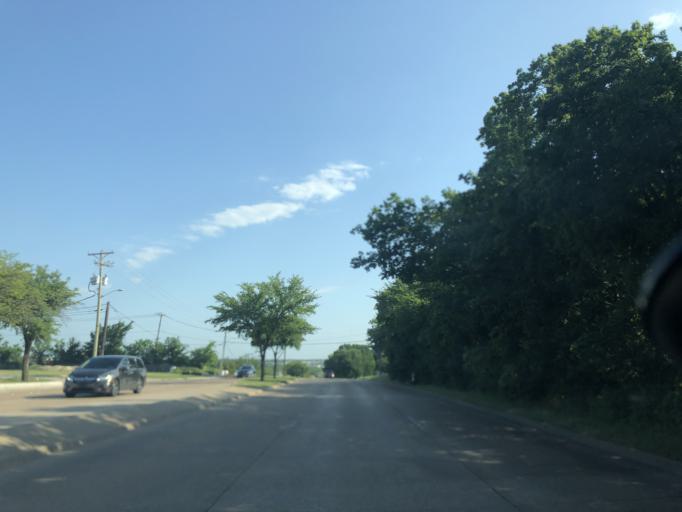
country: US
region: Texas
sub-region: Dallas County
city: Sunnyvale
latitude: 32.8234
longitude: -96.5957
